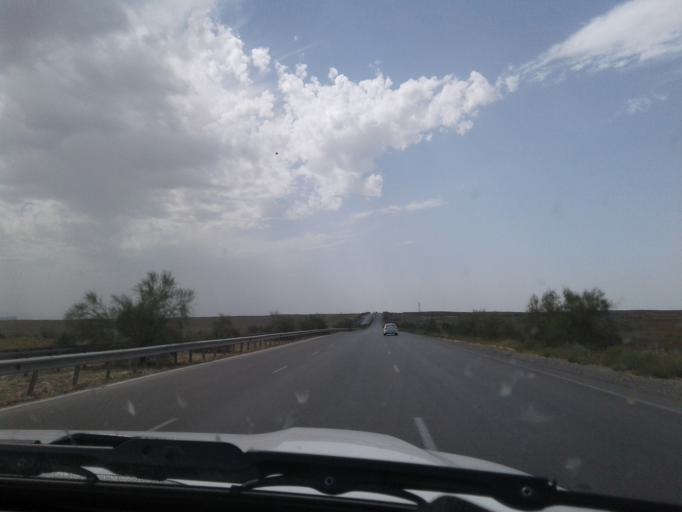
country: TM
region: Ahal
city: Annau
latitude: 37.8502
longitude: 58.7007
